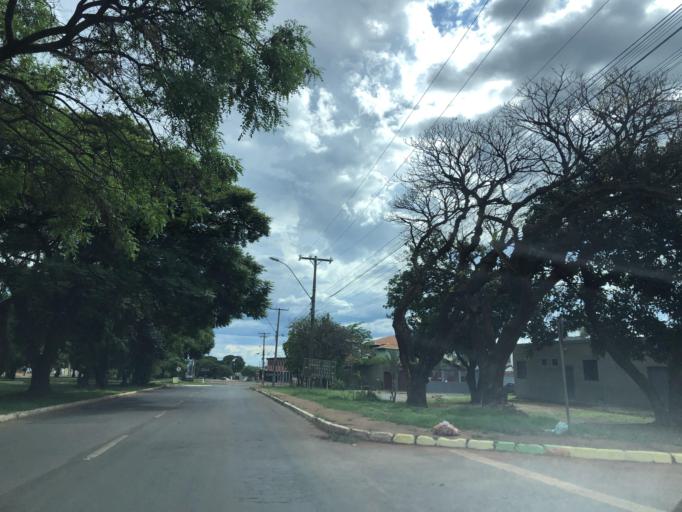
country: BR
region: Goias
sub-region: Luziania
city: Luziania
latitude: -16.0269
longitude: -48.0720
